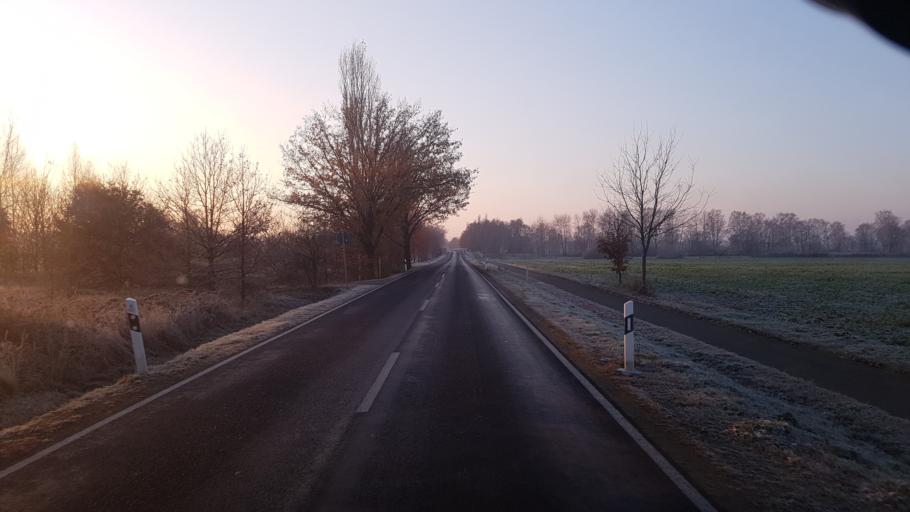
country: DE
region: Brandenburg
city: Tettau
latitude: 51.4629
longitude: 13.7399
